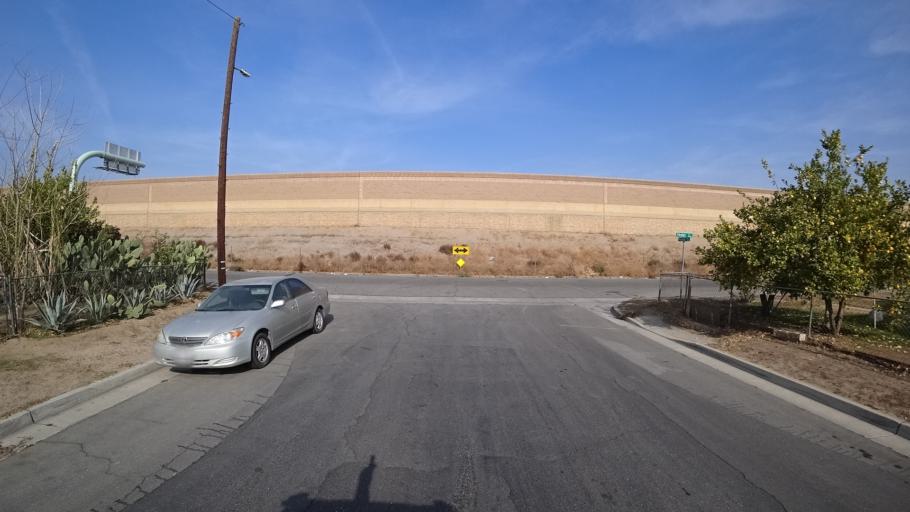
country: US
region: California
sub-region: Kern County
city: Bakersfield
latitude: 35.3519
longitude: -119.0129
